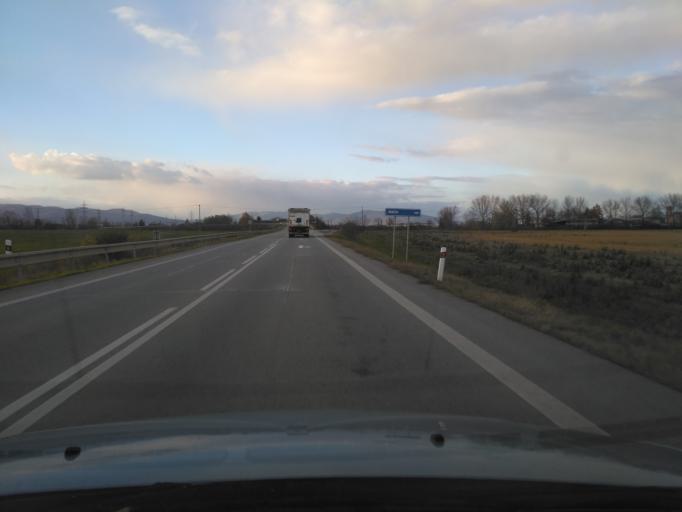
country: SK
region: Kosicky
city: Trebisov
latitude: 48.6213
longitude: 21.7014
